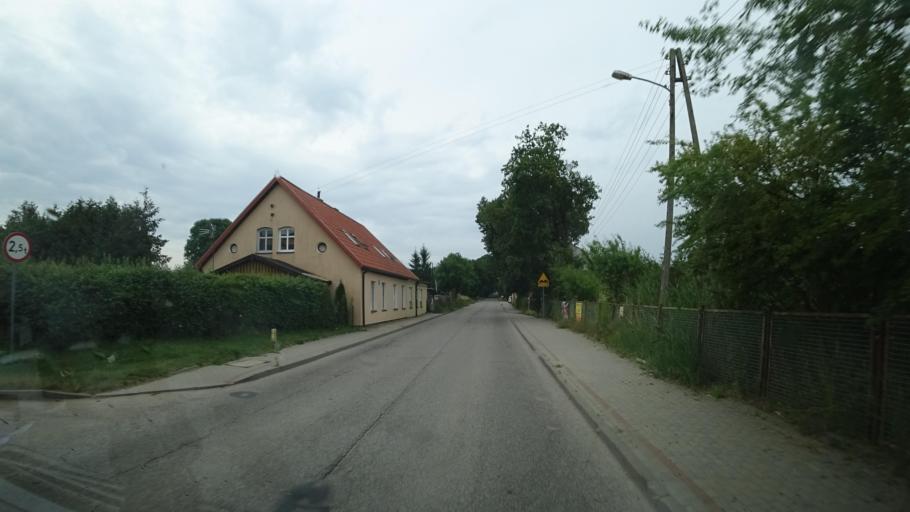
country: PL
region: Warmian-Masurian Voivodeship
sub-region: Powiat gizycki
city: Ryn
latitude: 53.9337
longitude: 21.5496
